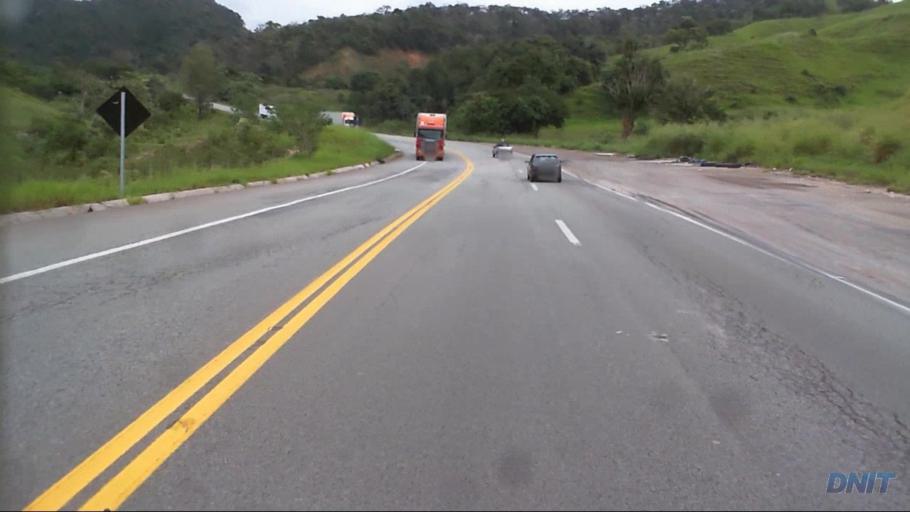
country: BR
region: Minas Gerais
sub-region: Timoteo
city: Timoteo
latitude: -19.6240
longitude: -42.8572
